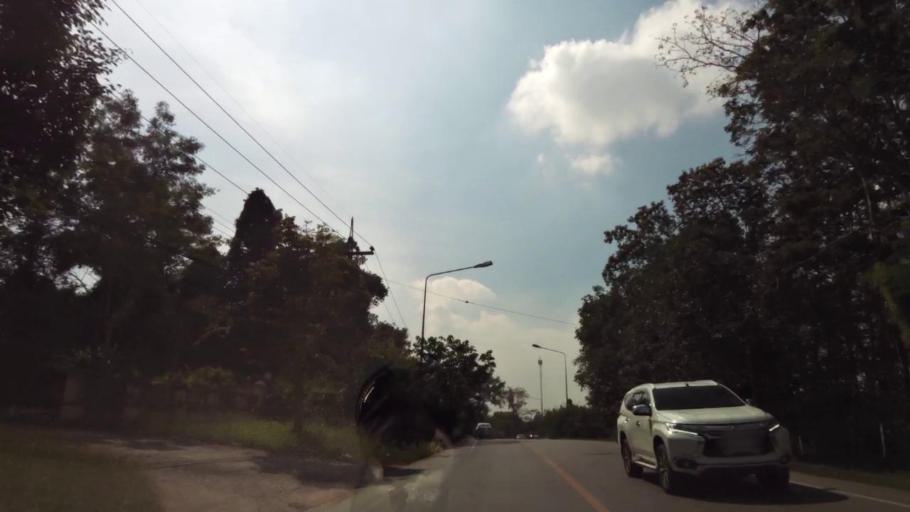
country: TH
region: Chiang Rai
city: Chiang Rai
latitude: 19.8703
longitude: 99.7794
